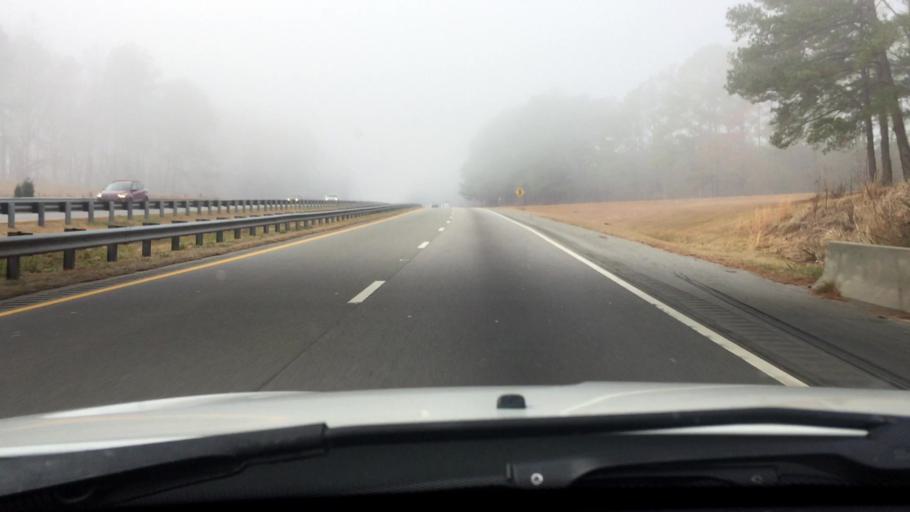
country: US
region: North Carolina
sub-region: Wake County
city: Holly Springs
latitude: 35.6690
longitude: -78.9307
